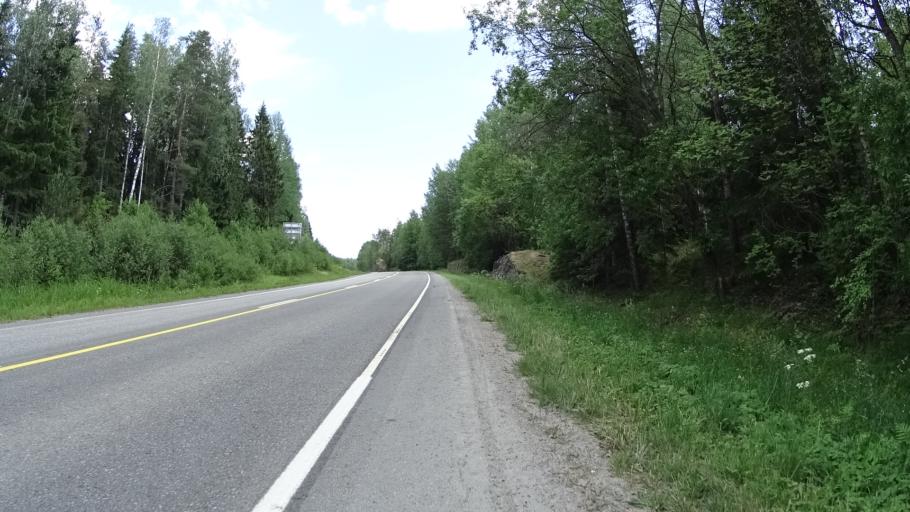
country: FI
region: Uusimaa
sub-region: Raaseporin
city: Pohja
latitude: 60.1034
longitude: 23.5669
